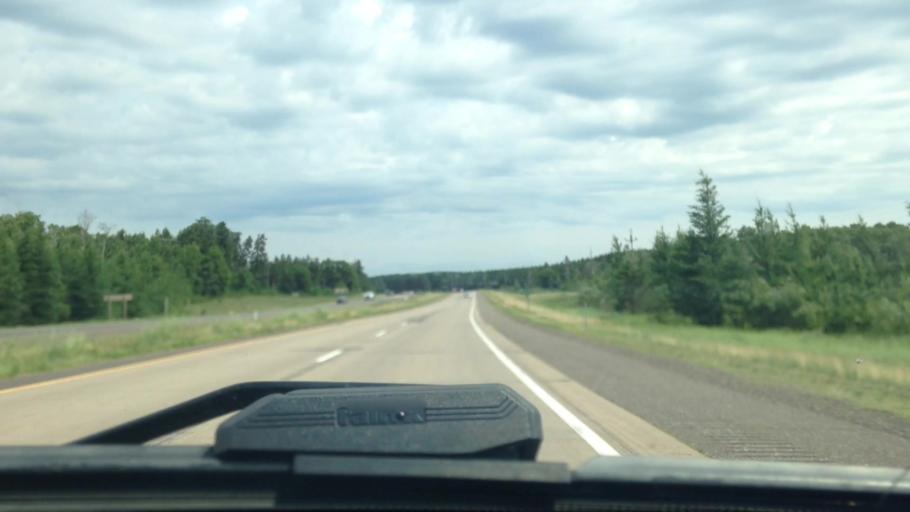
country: US
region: Wisconsin
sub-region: Douglas County
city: Lake Nebagamon
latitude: 46.1780
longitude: -91.8024
